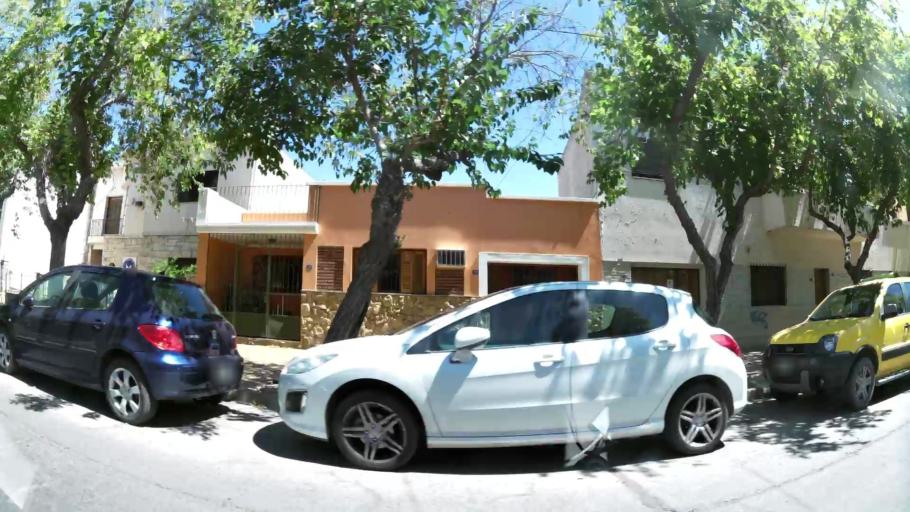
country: AR
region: San Juan
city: San Juan
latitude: -31.5321
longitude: -68.5220
